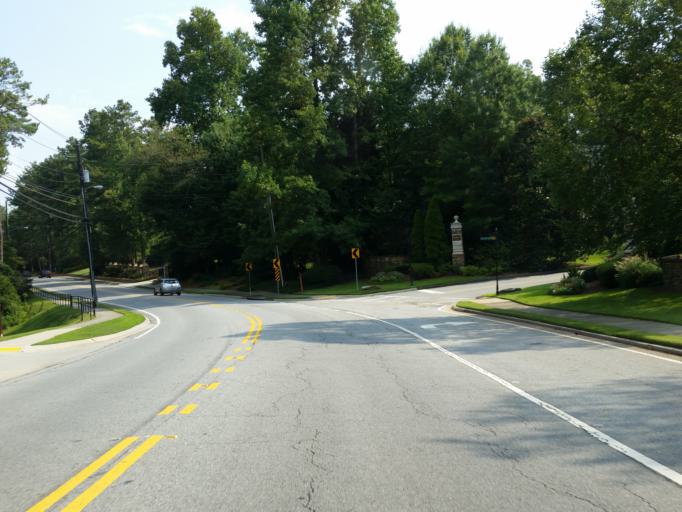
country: US
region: Georgia
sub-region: DeKalb County
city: North Atlanta
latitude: 33.8968
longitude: -84.3526
